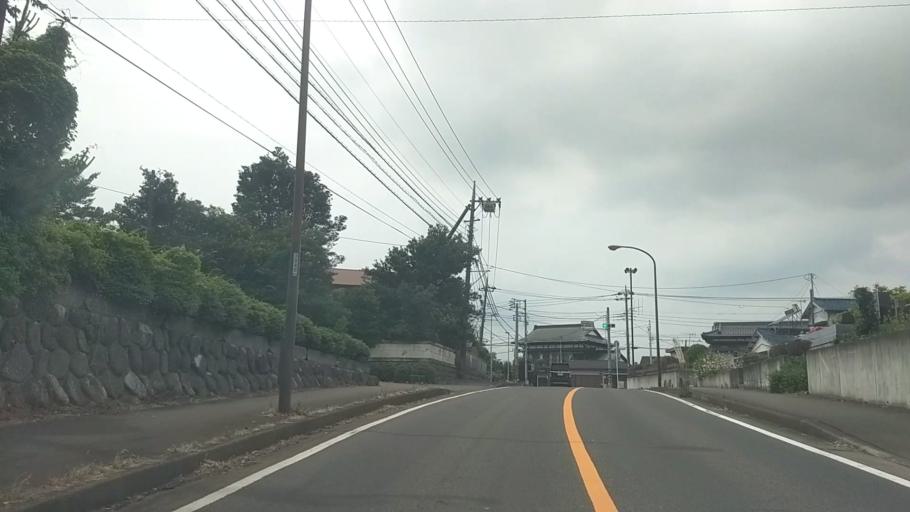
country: JP
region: Kanagawa
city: Chigasaki
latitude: 35.3853
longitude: 139.4135
